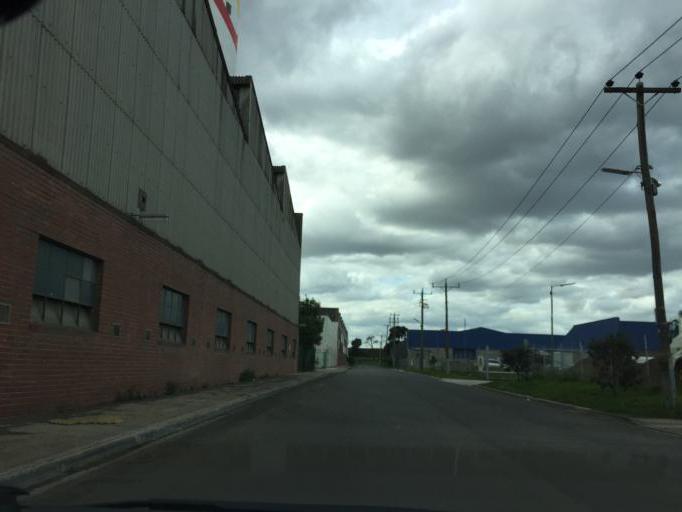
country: AU
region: Victoria
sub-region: Maribyrnong
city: Braybrook
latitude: -37.8014
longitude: 144.8574
